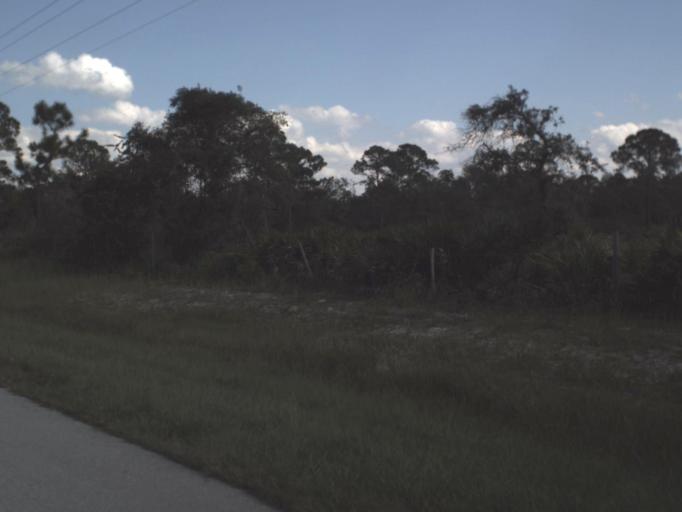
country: US
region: Florida
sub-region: Highlands County
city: Sebring
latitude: 27.4204
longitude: -81.4379
